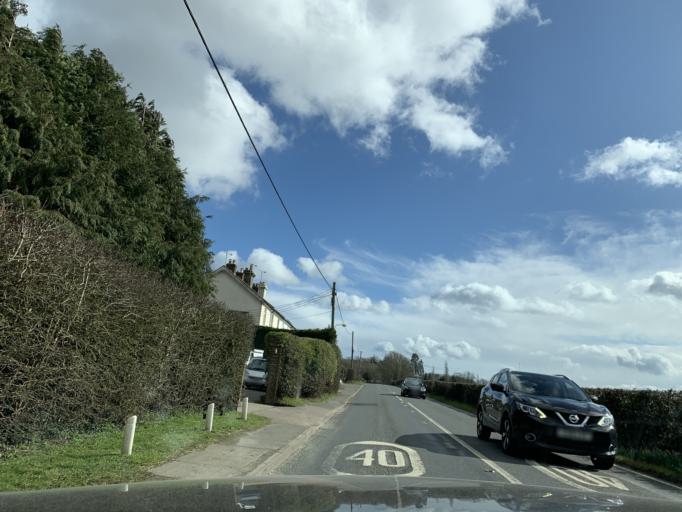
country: GB
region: England
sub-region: West Sussex
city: Crawley Down
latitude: 51.0974
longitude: -0.0830
